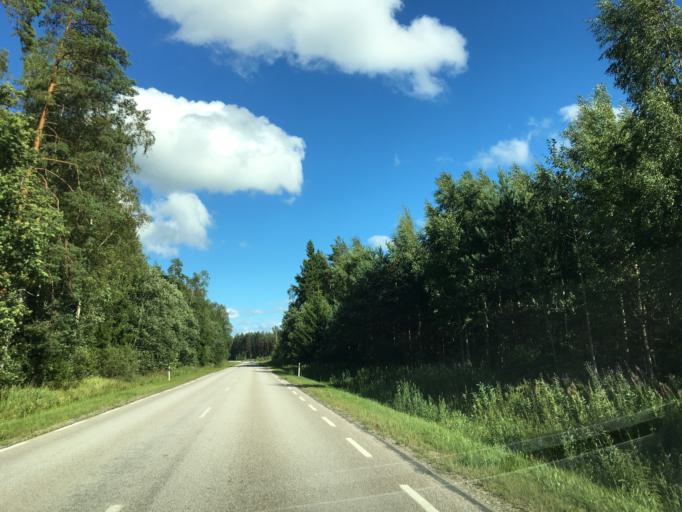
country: EE
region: Paernumaa
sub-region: Vaendra vald (alev)
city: Vandra
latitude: 58.5790
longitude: 25.2367
